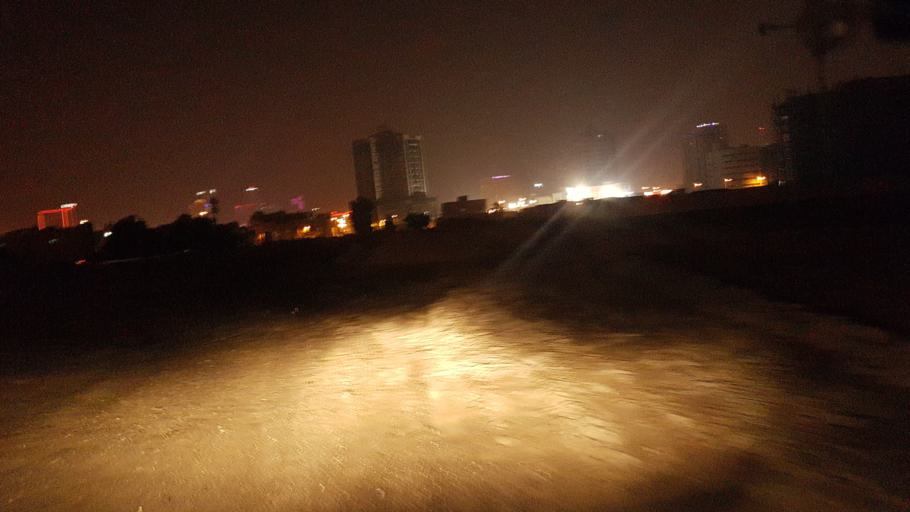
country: BH
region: Manama
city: Jidd Hafs
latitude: 26.2229
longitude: 50.5392
